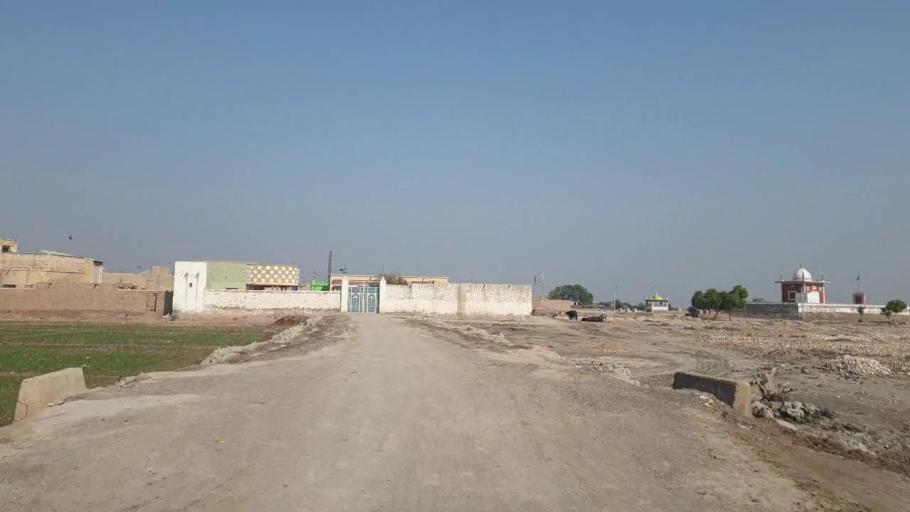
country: PK
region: Sindh
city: Bhan
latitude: 26.4393
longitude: 67.7313
